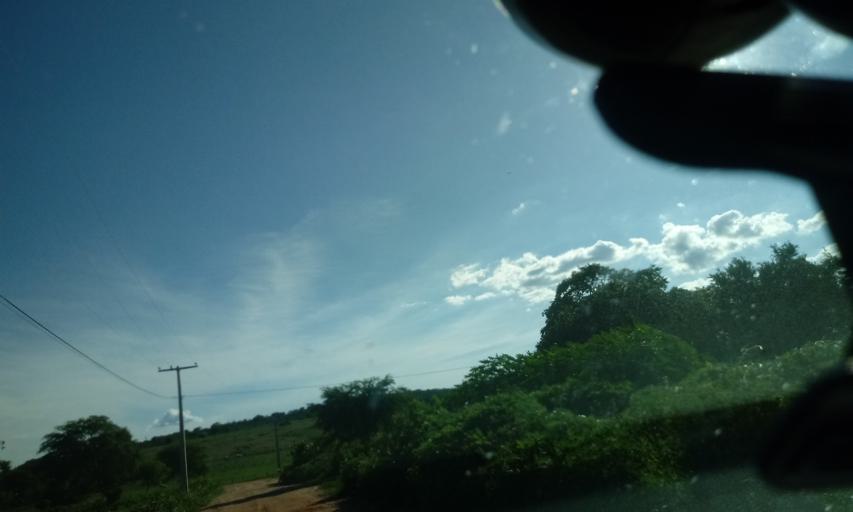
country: BR
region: Bahia
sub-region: Riacho De Santana
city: Riacho de Santana
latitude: -13.8156
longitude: -42.7634
